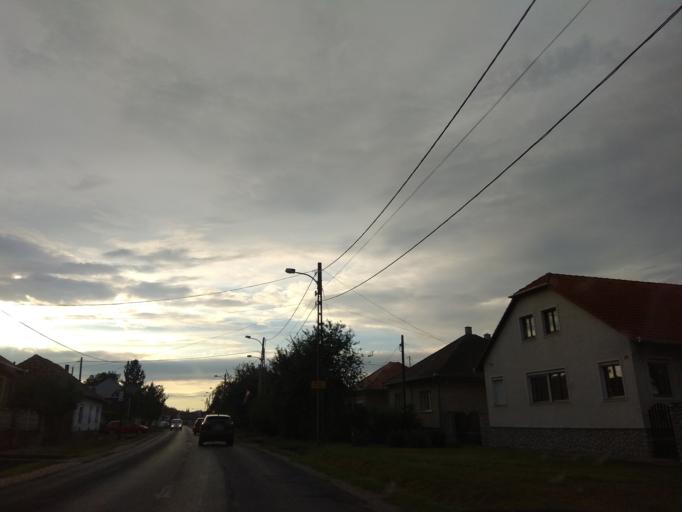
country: HU
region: Borsod-Abauj-Zemplen
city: Miskolc
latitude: 48.0894
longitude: 20.8129
